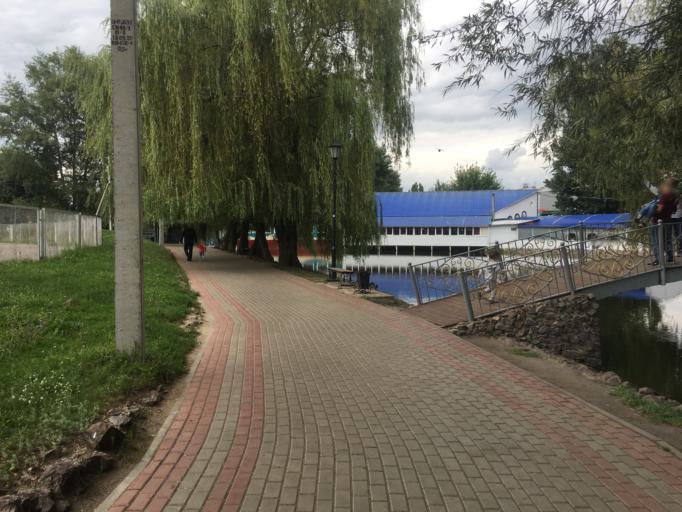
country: RU
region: Voronezj
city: Rossosh'
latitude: 50.1972
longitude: 39.5759
